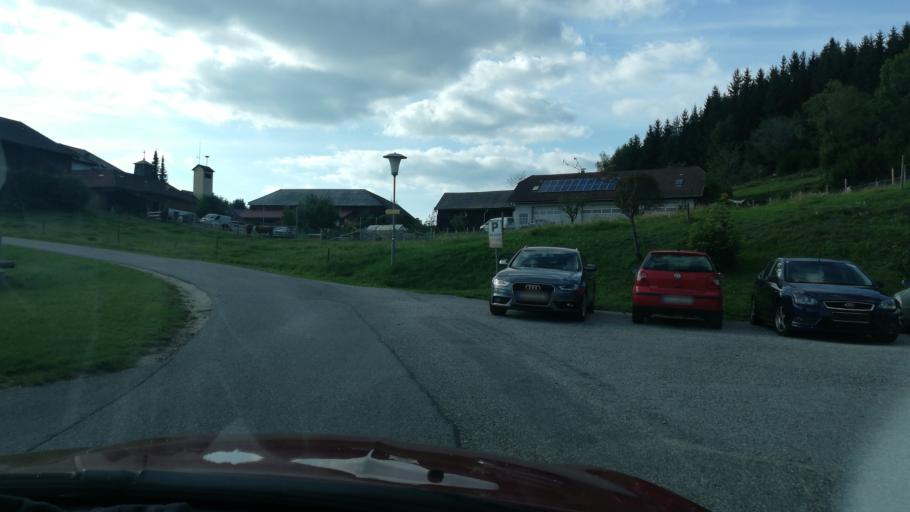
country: AT
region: Lower Austria
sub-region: Politischer Bezirk Zwettl
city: Langschlag
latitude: 48.4776
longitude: 14.8150
